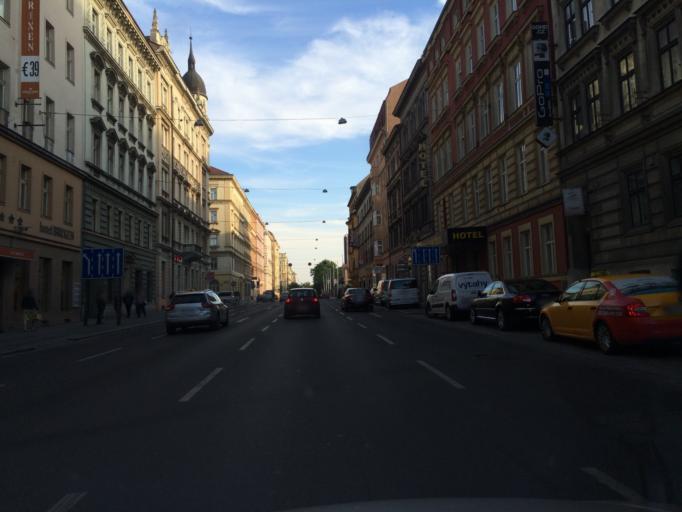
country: CZ
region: Praha
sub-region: Praha 2
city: Vysehrad
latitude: 50.0743
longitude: 14.4291
